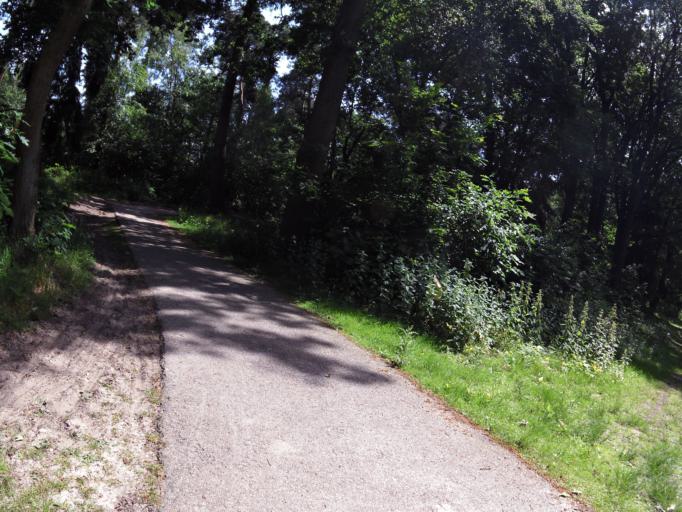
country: NL
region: North Brabant
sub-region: Gemeente Son en Breugel
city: Son
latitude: 51.5168
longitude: 5.4674
